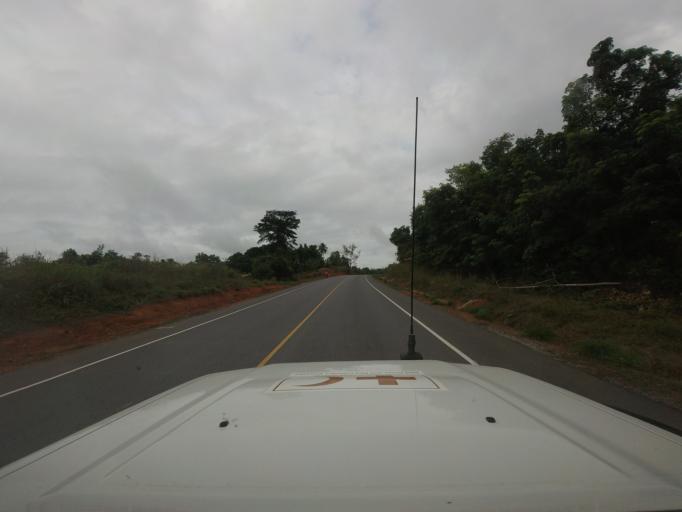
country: LR
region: Bong
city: Gbarnga
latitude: 7.0024
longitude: -9.4178
